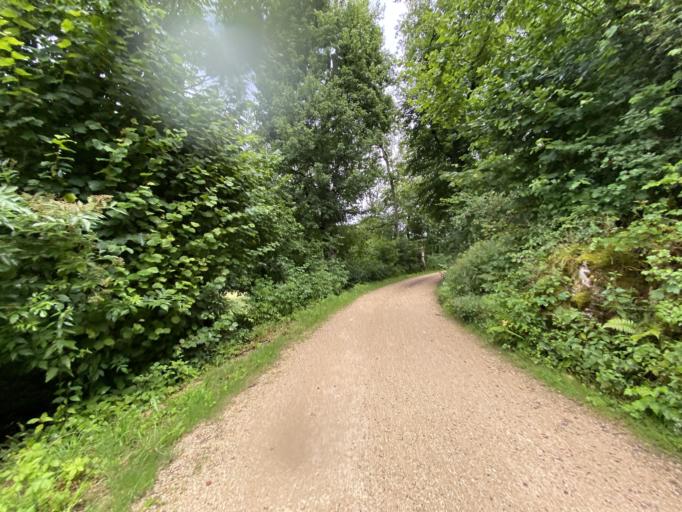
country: DE
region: Baden-Wuerttemberg
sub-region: Tuebingen Region
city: Sigmaringen
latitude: 48.1159
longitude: 9.2189
